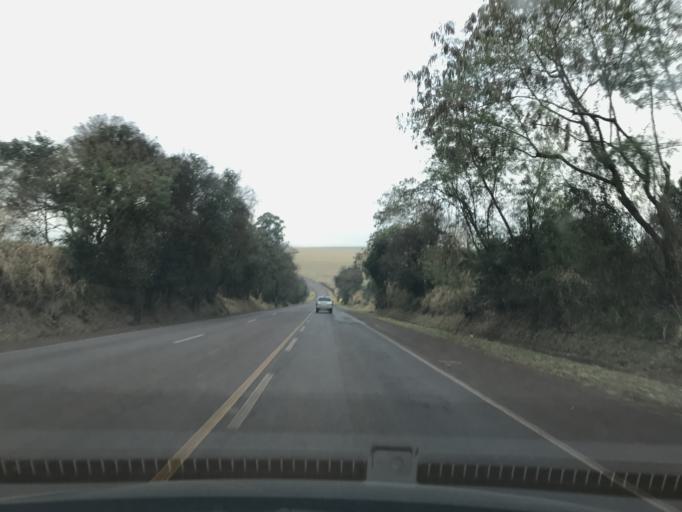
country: BR
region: Parana
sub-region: Toledo
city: Toledo
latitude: -24.6330
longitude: -53.7119
